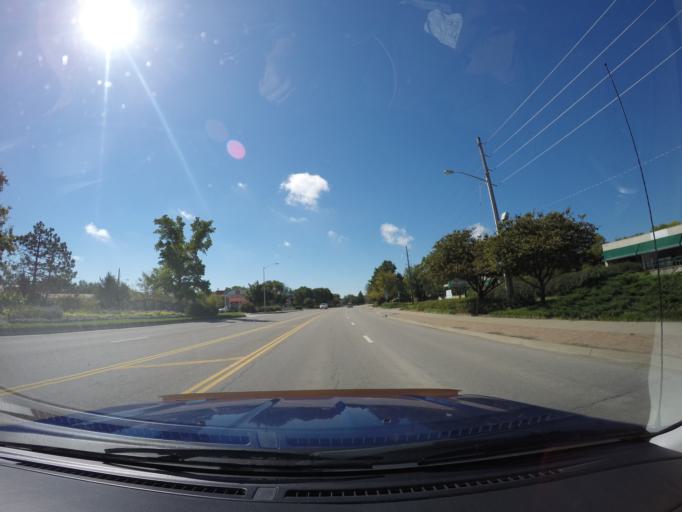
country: US
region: Kansas
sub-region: Douglas County
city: Lawrence
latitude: 38.9877
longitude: -95.2336
